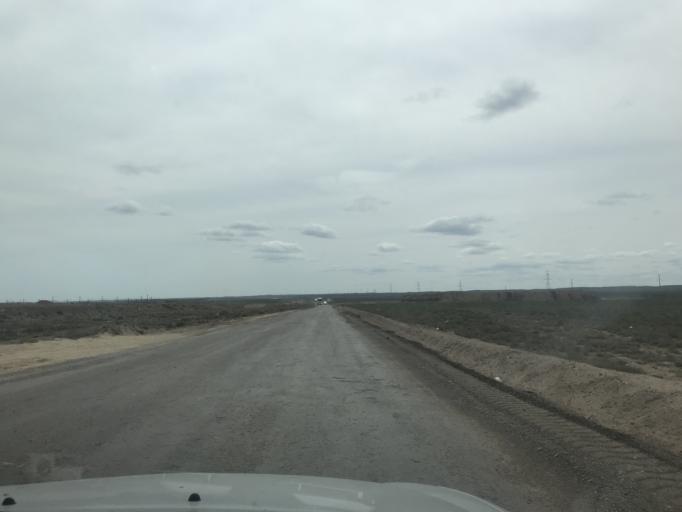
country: KZ
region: Almaty Oblysy
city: Ulken
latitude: 45.2621
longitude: 73.7982
